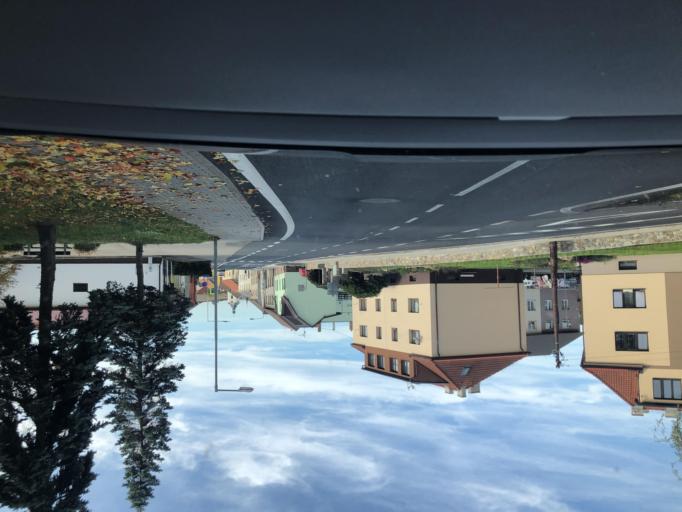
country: CZ
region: Central Bohemia
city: Divisov
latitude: 49.7906
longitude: 14.8713
